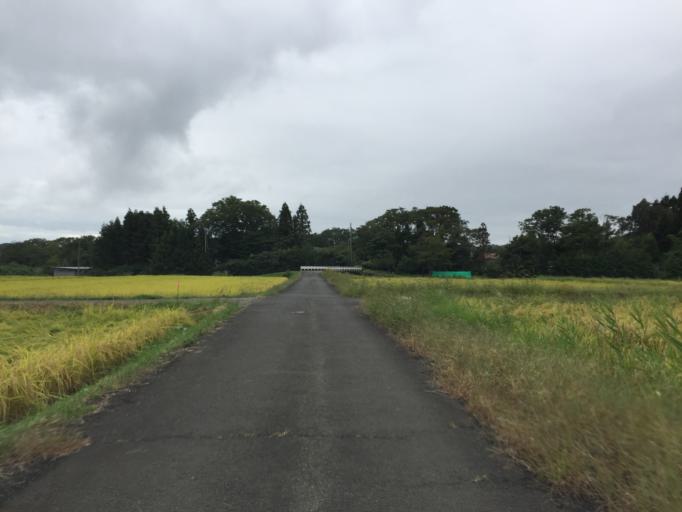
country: JP
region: Fukushima
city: Nihommatsu
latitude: 37.6566
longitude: 140.4476
